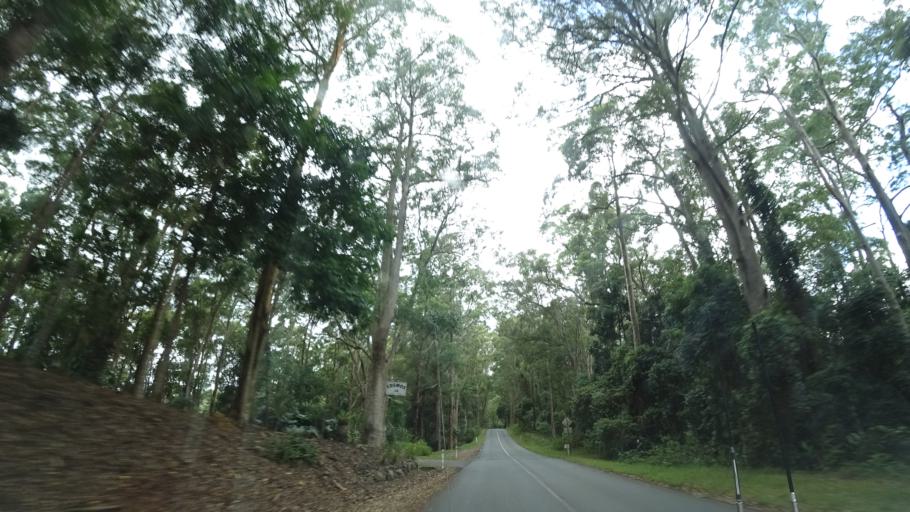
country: AU
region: Queensland
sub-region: Moreton Bay
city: Highvale
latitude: -27.3998
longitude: 152.7970
